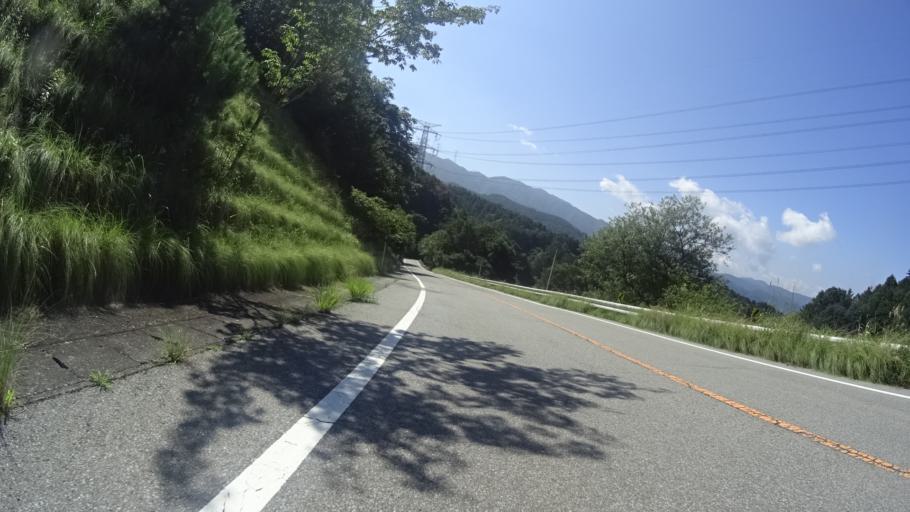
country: JP
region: Yamanashi
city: Enzan
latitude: 35.7462
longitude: 138.8082
